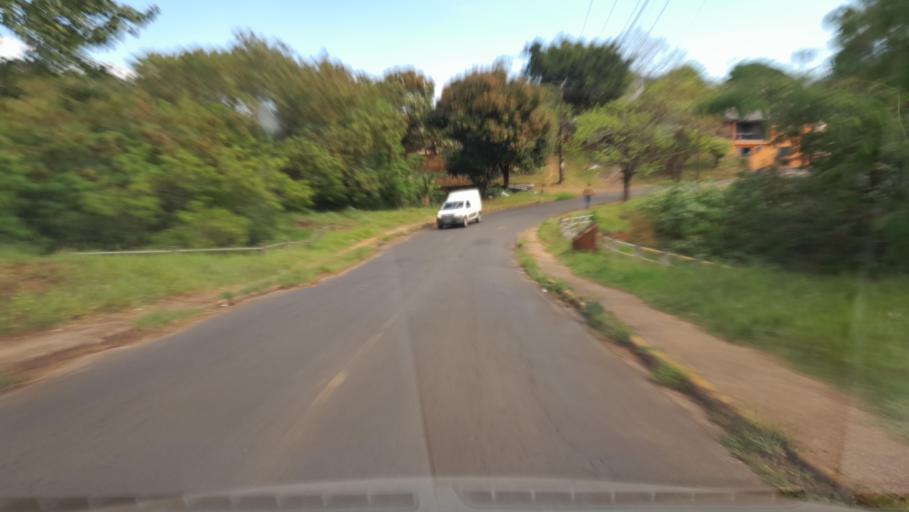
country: BR
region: Parana
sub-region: Umuarama
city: Umuarama
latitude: -23.7723
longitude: -53.3039
